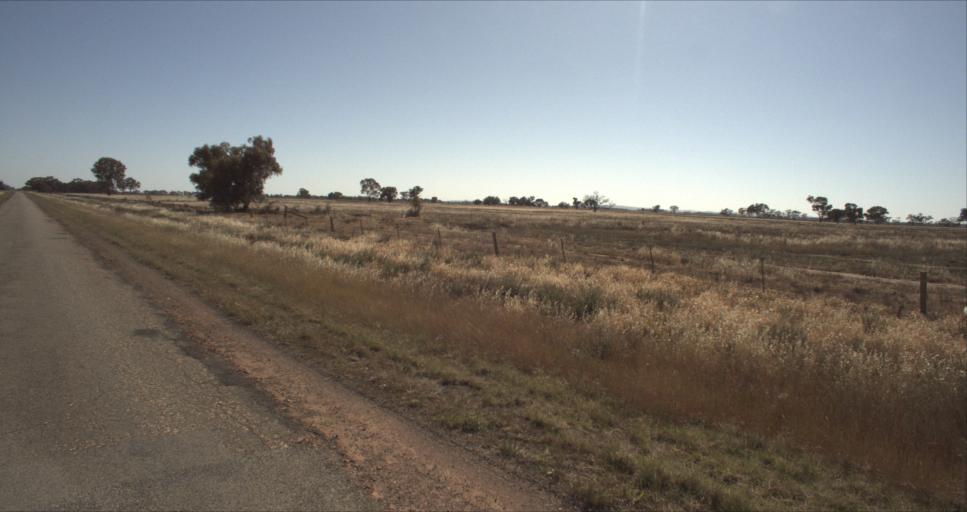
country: AU
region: New South Wales
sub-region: Leeton
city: Leeton
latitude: -34.5974
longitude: 146.2584
